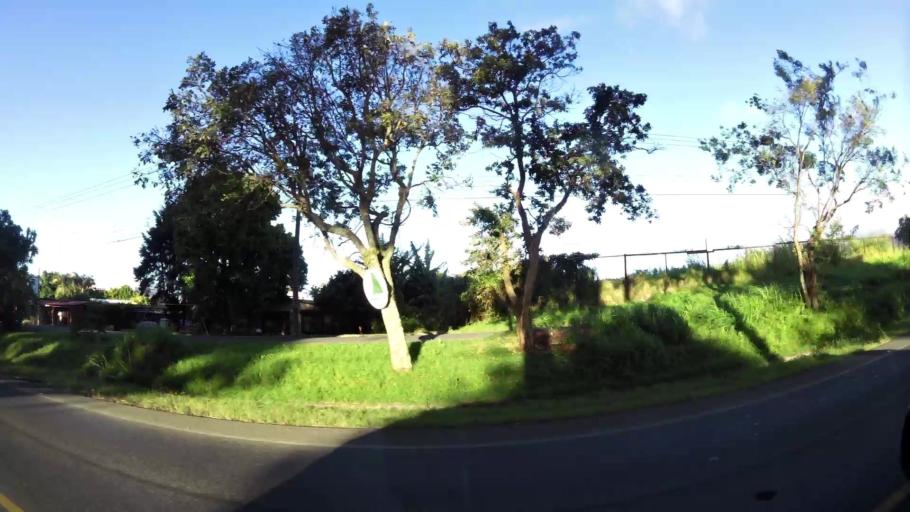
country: CR
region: Heredia
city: Angeles
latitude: 9.9963
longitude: -84.0360
